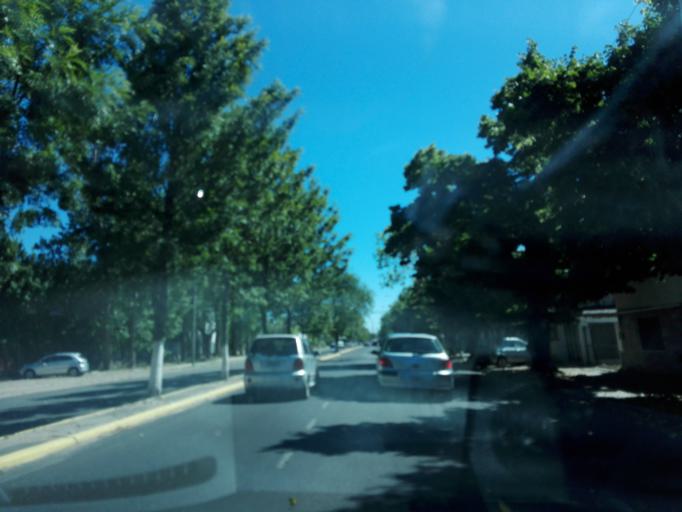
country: AR
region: Buenos Aires
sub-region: Partido de La Plata
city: La Plata
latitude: -34.9048
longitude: -57.9246
